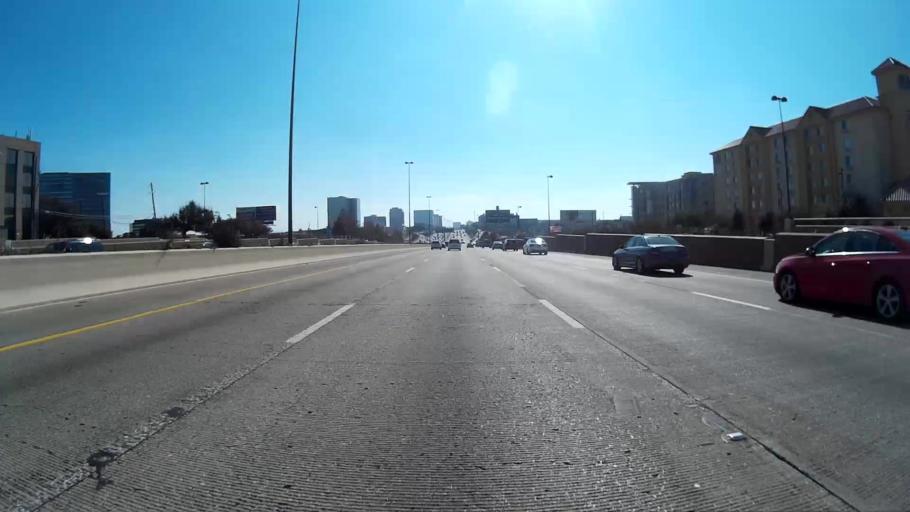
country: US
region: Texas
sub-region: Dallas County
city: University Park
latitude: 32.8836
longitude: -96.7703
